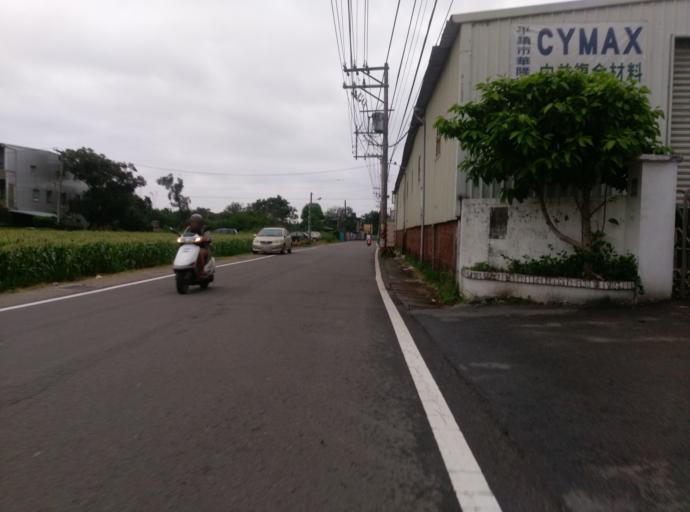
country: TW
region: Taiwan
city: Daxi
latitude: 24.9136
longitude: 121.2386
